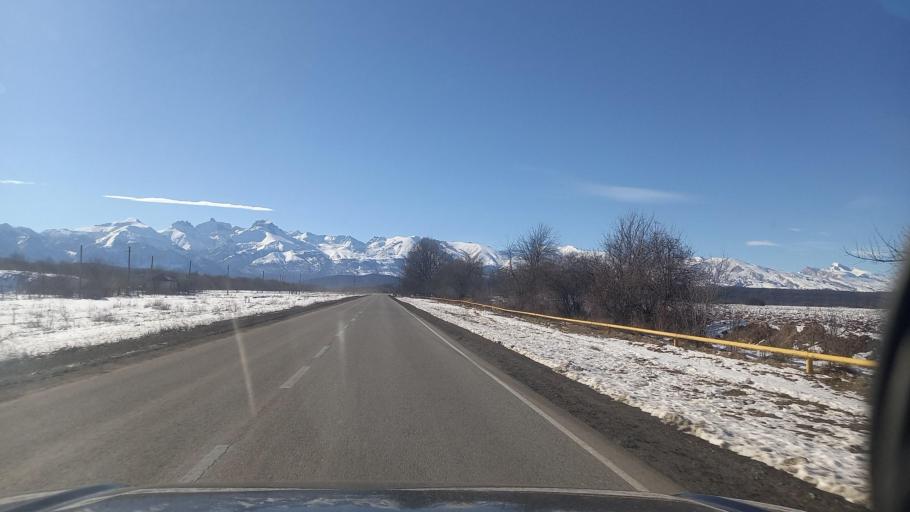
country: RU
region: North Ossetia
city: Chikola
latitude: 43.1722
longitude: 43.8704
